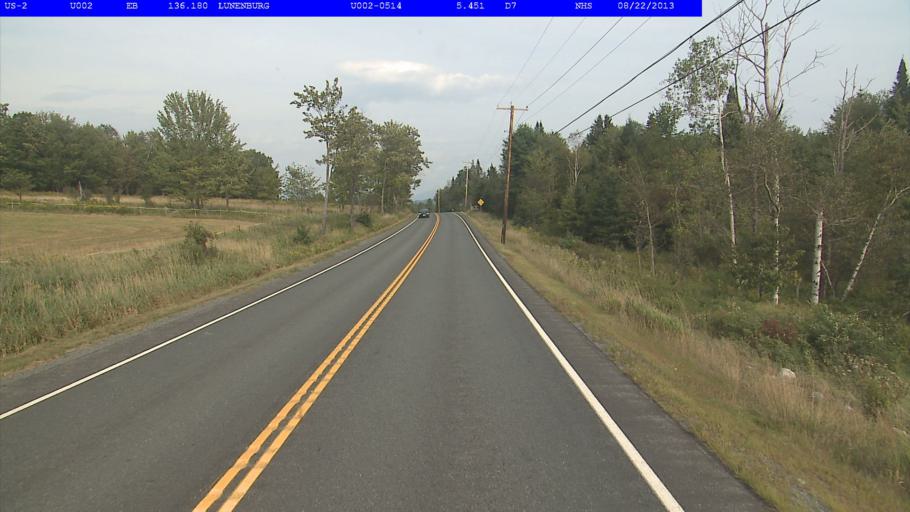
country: US
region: New Hampshire
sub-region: Coos County
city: Lancaster
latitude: 44.4642
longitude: -71.6672
